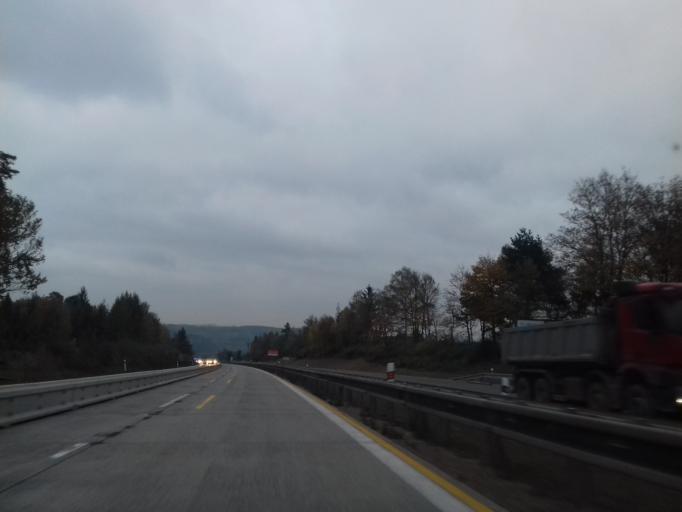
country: CZ
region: Central Bohemia
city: Trhovy Stepanov
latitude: 49.7501
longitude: 15.0013
